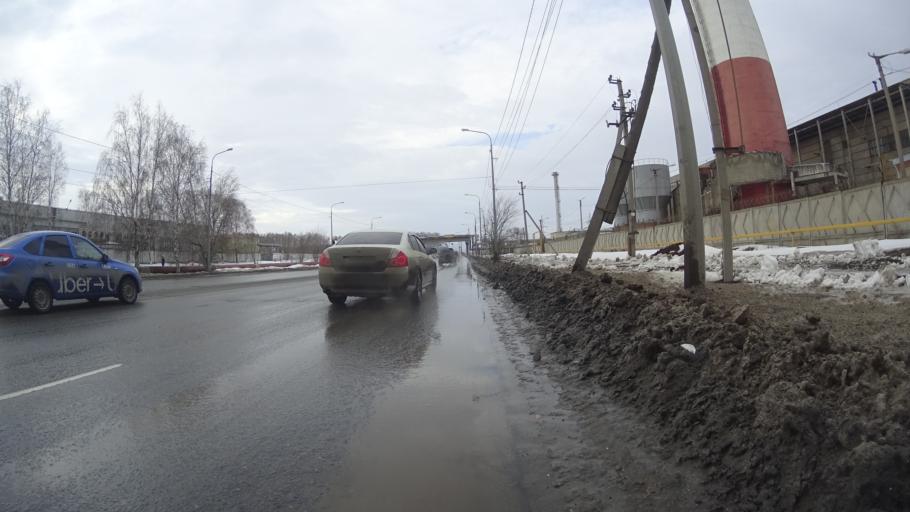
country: RU
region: Chelyabinsk
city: Roshchino
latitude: 55.2066
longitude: 61.3202
